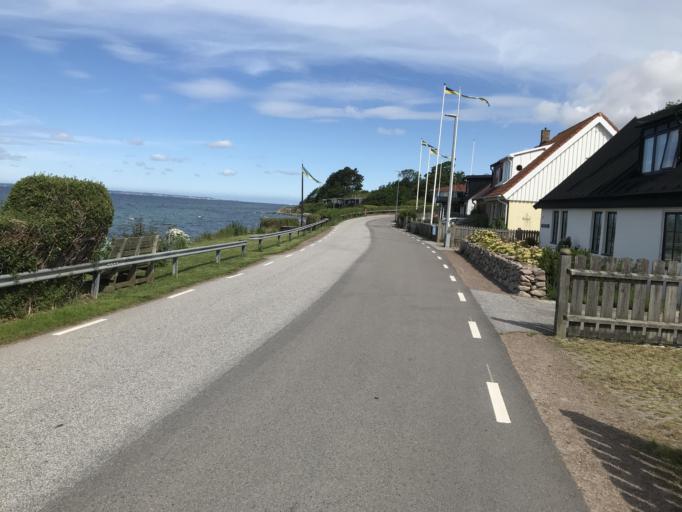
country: SE
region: Skane
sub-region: Helsingborg
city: Rydeback
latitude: 55.9418
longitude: 12.7719
